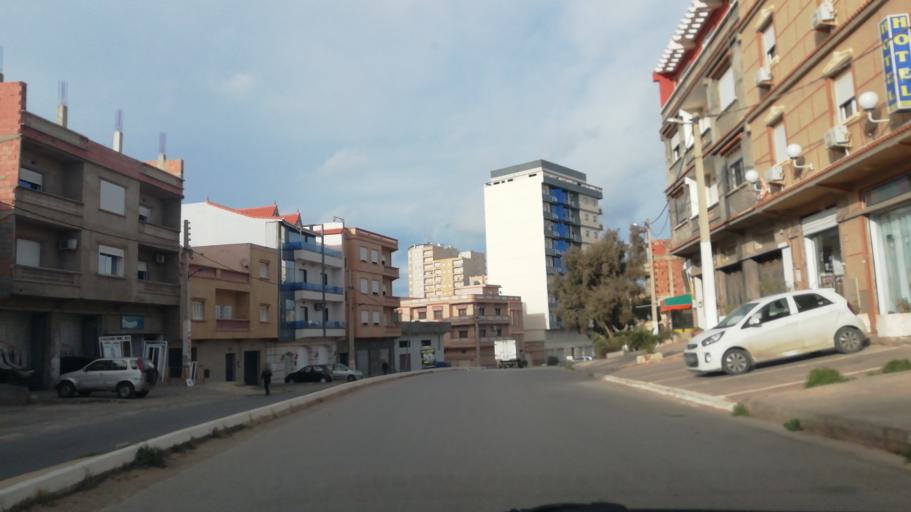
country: DZ
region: Oran
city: Bir el Djir
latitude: 35.7351
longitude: -0.5725
